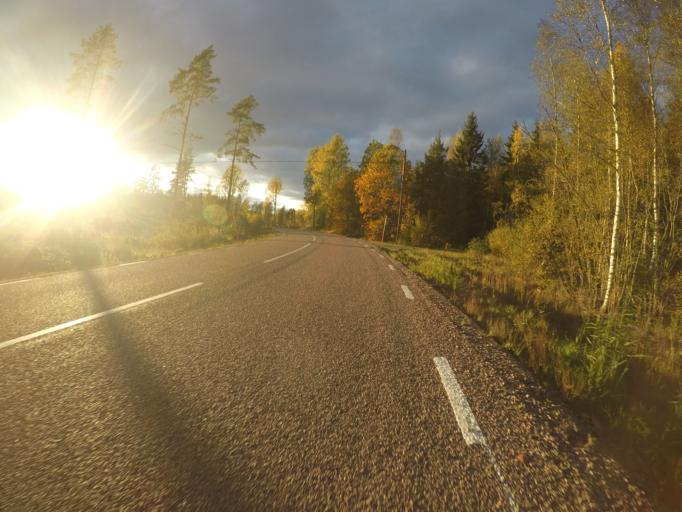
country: SE
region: Vaestmanland
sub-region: Arboga Kommun
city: Tyringe
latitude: 59.3096
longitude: 15.9923
